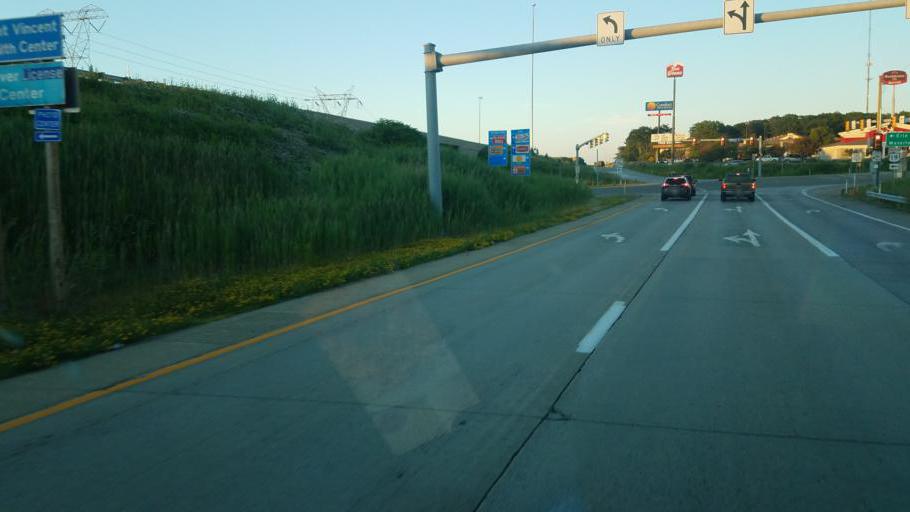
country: US
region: Pennsylvania
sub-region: Erie County
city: Erie
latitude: 42.0488
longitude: -80.0819
